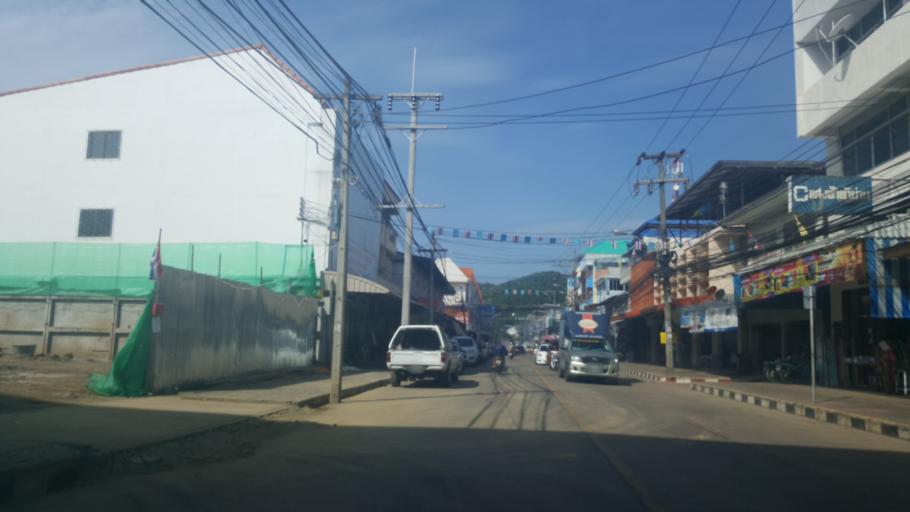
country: TH
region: Chon Buri
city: Sattahip
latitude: 12.6651
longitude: 100.9001
